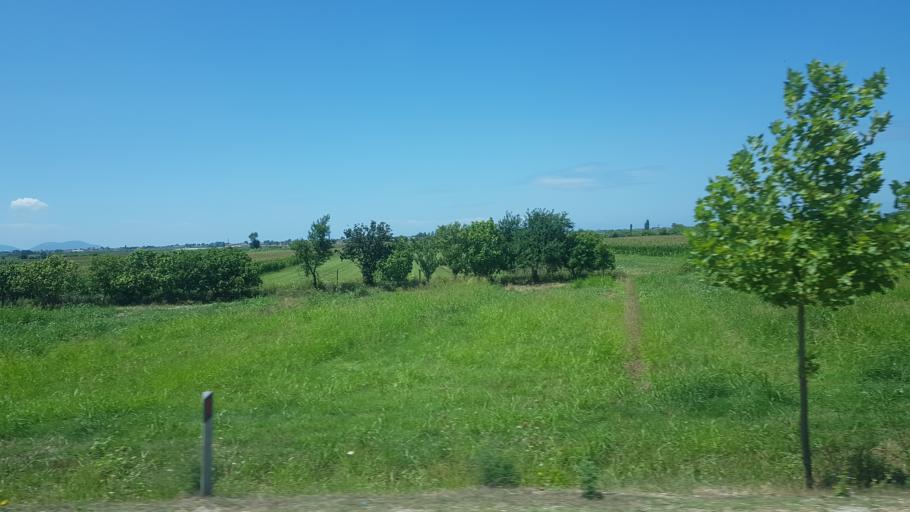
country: AL
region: Fier
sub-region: Rrethi i Fierit
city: Frakulla e Madhe
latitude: 40.6613
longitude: 19.4891
